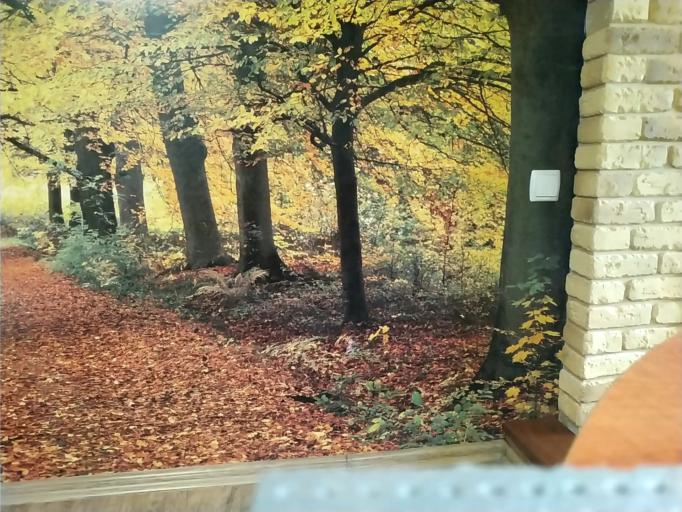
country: RU
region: Tverskaya
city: Staritsa
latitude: 56.5373
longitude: 34.9881
